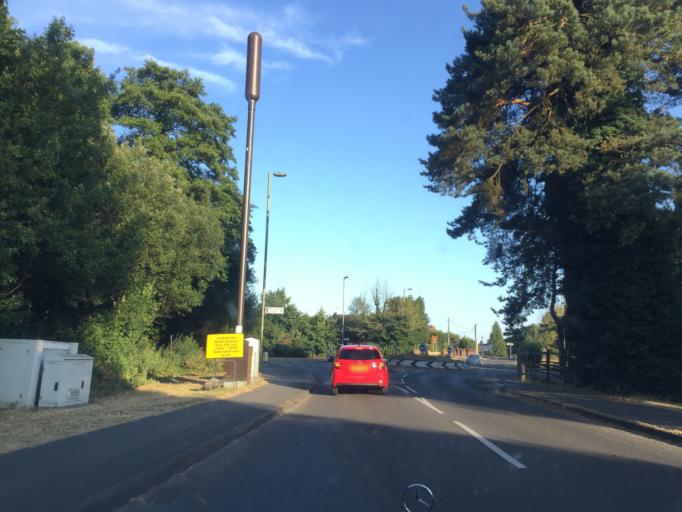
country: GB
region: England
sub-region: Surrey
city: Frimley
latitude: 51.3108
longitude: -0.7347
